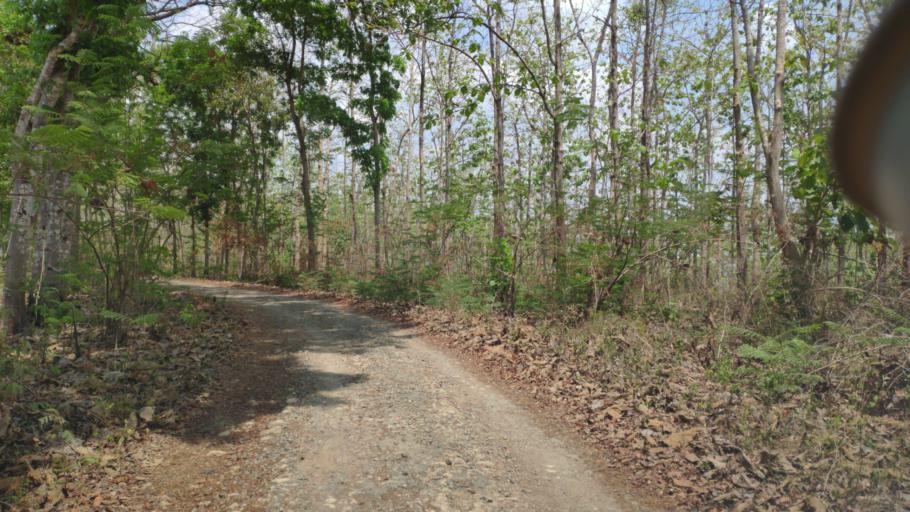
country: ID
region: Central Java
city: Singonegoro
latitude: -6.9906
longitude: 111.5415
